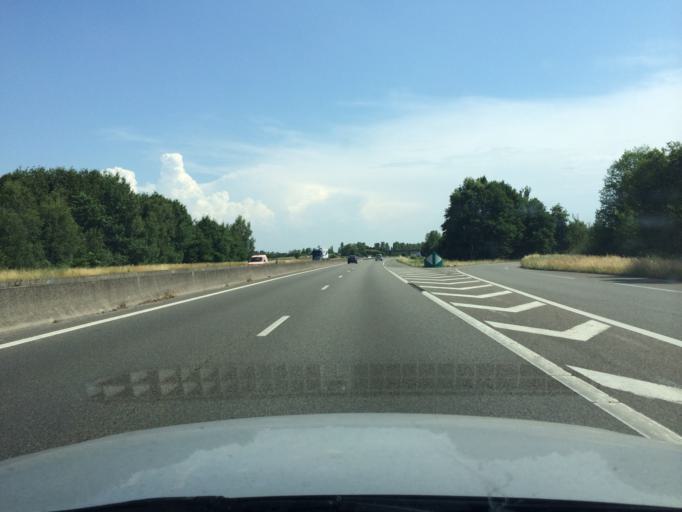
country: FR
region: Alsace
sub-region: Departement du Bas-Rhin
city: Vendenheim
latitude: 48.6783
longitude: 7.7340
